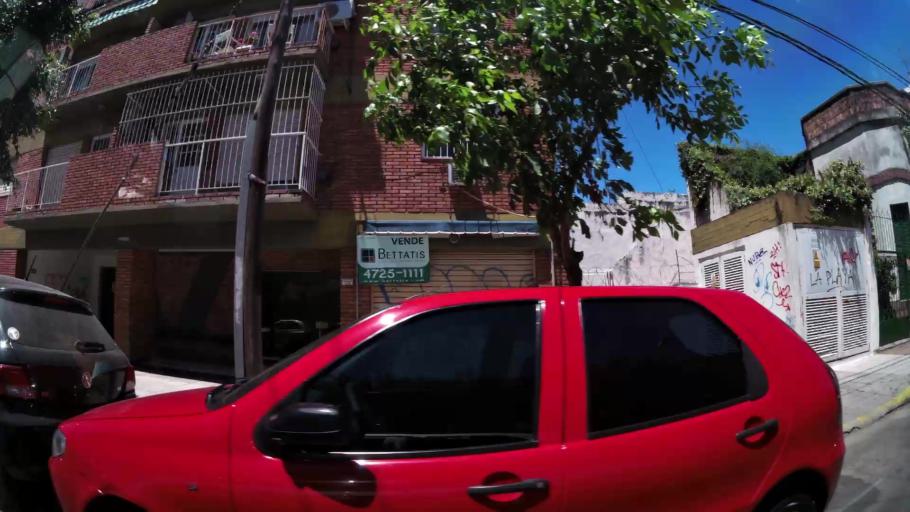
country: AR
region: Buenos Aires
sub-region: Partido de Tigre
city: Tigre
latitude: -34.4432
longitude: -58.5543
